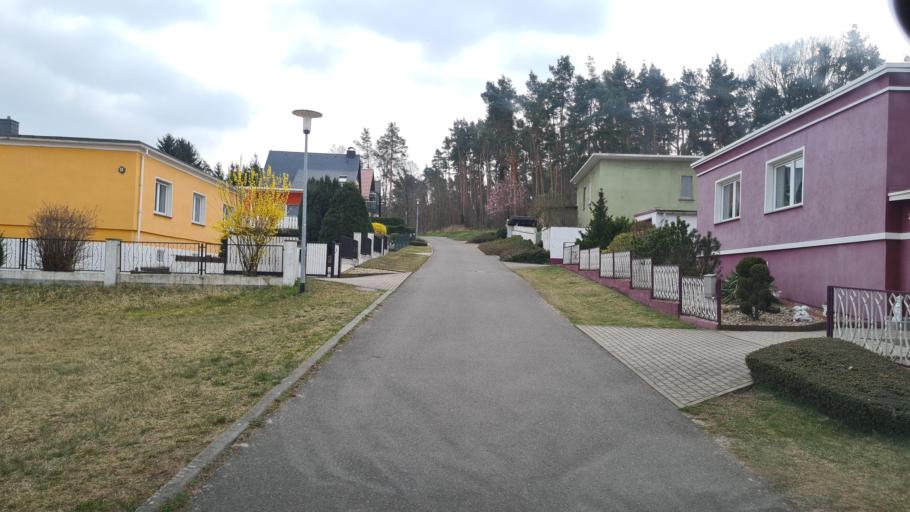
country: DE
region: Brandenburg
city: Merzdorf
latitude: 51.4044
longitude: 13.5493
